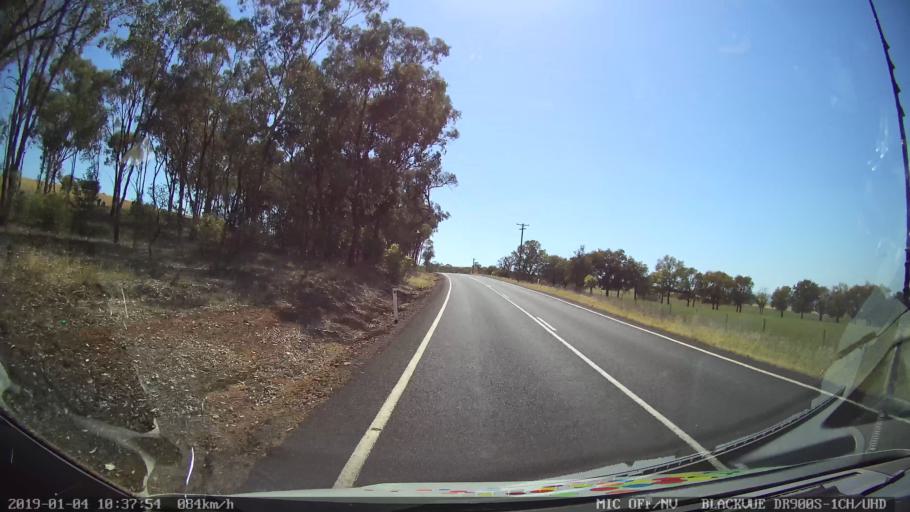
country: AU
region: New South Wales
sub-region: Cabonne
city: Molong
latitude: -33.2949
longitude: 148.7016
